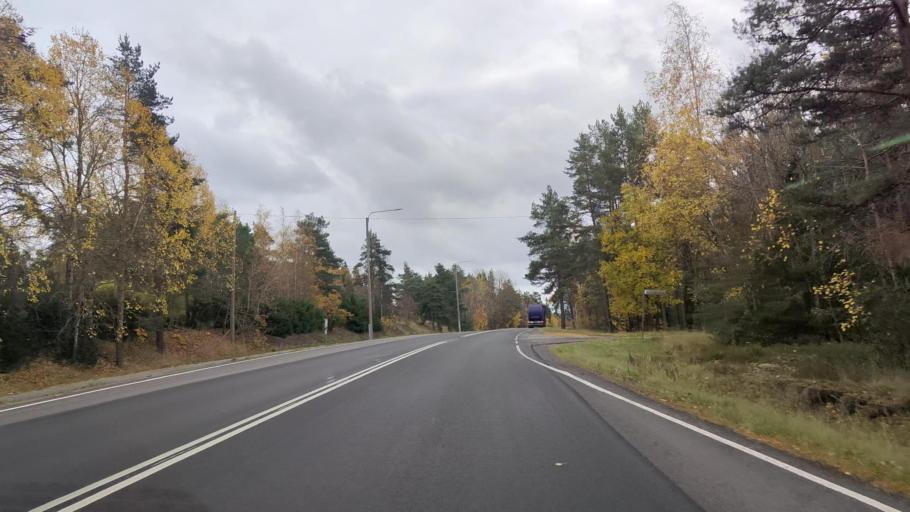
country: FI
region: Varsinais-Suomi
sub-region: Turku
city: Kaarina
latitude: 60.4514
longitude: 22.3720
